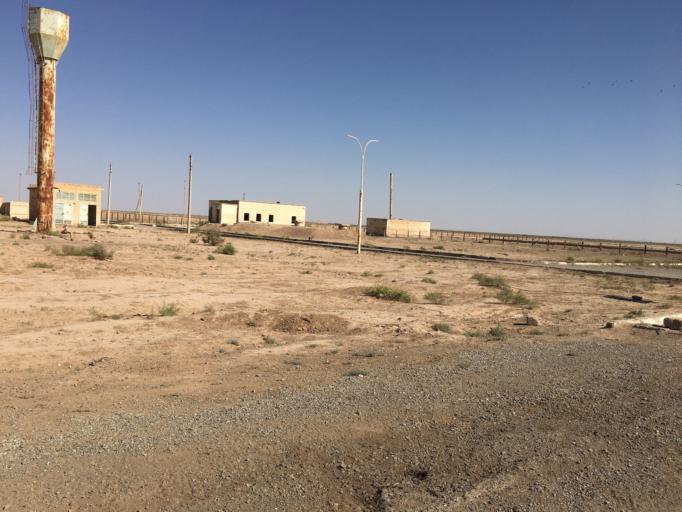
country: IR
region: Razavi Khorasan
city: Sarakhs
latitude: 36.4923
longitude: 61.2548
